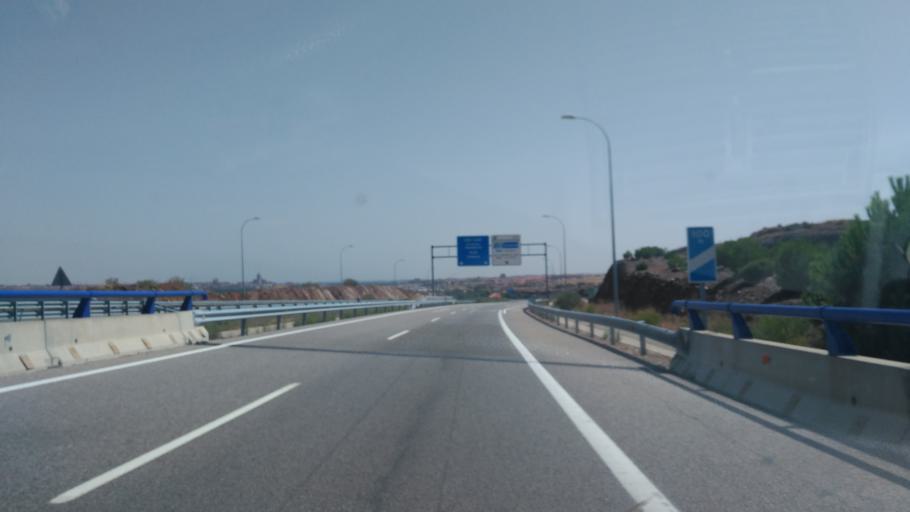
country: ES
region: Castille and Leon
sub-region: Provincia de Salamanca
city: Doninos de Salamanca
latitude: 40.9568
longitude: -5.7184
